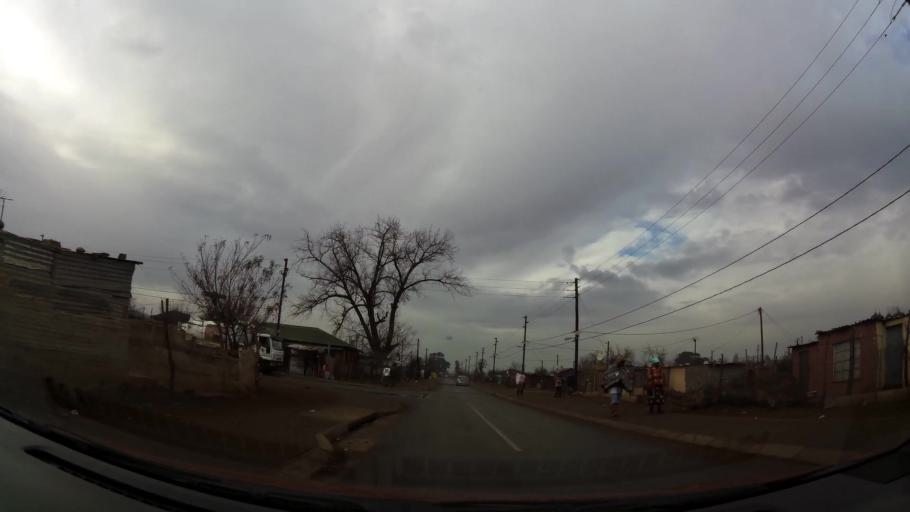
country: ZA
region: Gauteng
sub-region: City of Johannesburg Metropolitan Municipality
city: Soweto
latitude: -26.2851
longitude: 27.8377
